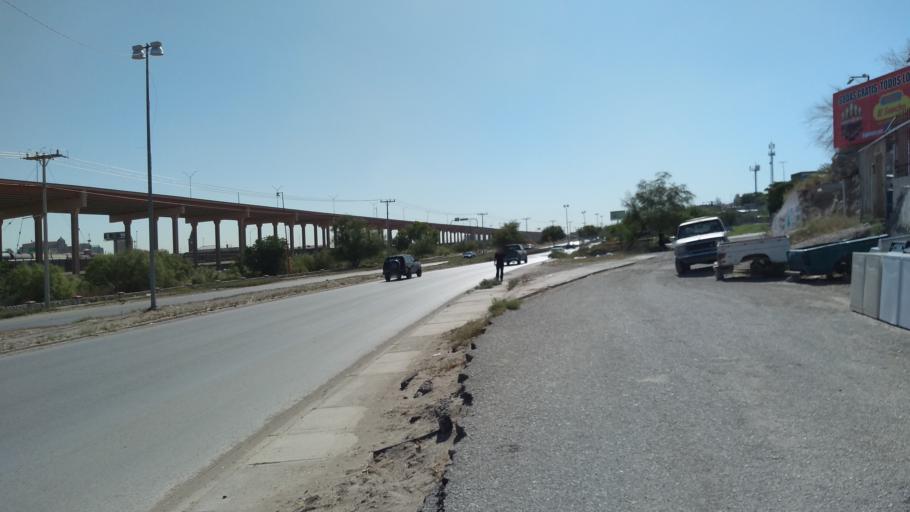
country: US
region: Texas
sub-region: El Paso County
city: El Paso
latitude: 31.7587
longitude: -106.5051
